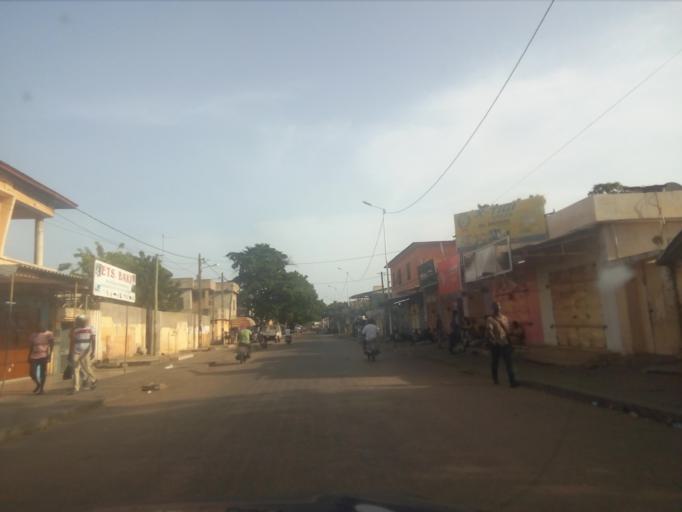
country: TG
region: Maritime
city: Lome
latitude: 6.1354
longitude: 1.2277
